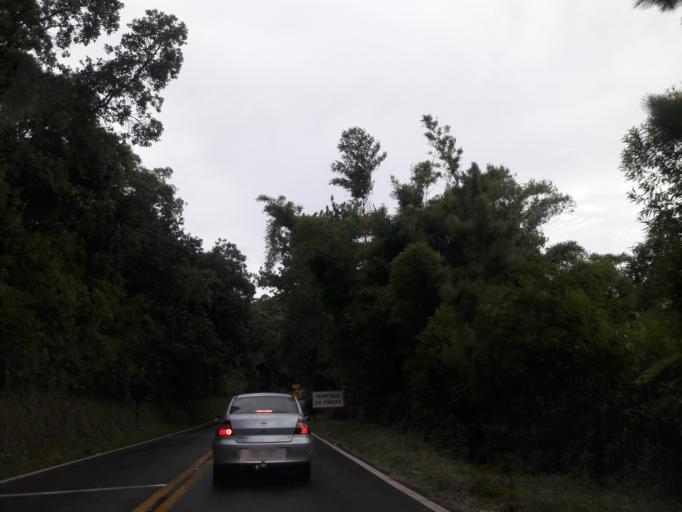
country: BR
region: Sao Paulo
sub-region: Aruja
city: Aruja
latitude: -23.3363
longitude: -46.4344
